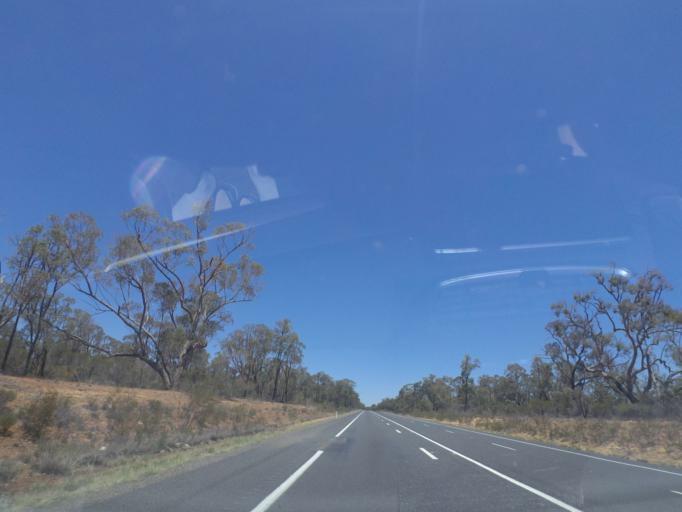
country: AU
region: New South Wales
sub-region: Warrumbungle Shire
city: Coonabarabran
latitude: -30.8729
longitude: 149.4494
